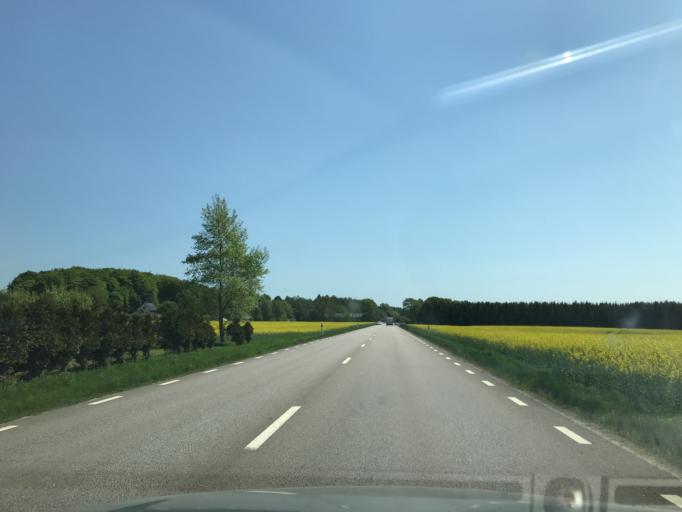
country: SE
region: Skane
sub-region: Angelholms Kommun
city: Munka-Ljungby
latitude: 56.2447
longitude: 13.0210
